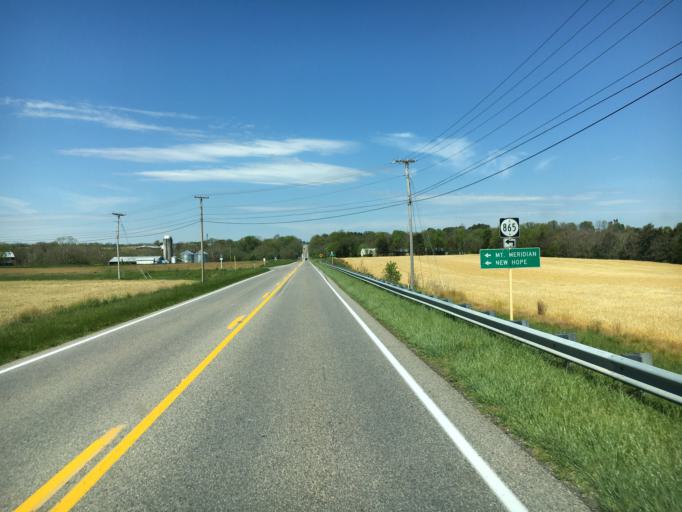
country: US
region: Virginia
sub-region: Rockingham County
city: Grottoes
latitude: 38.2666
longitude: -78.8575
